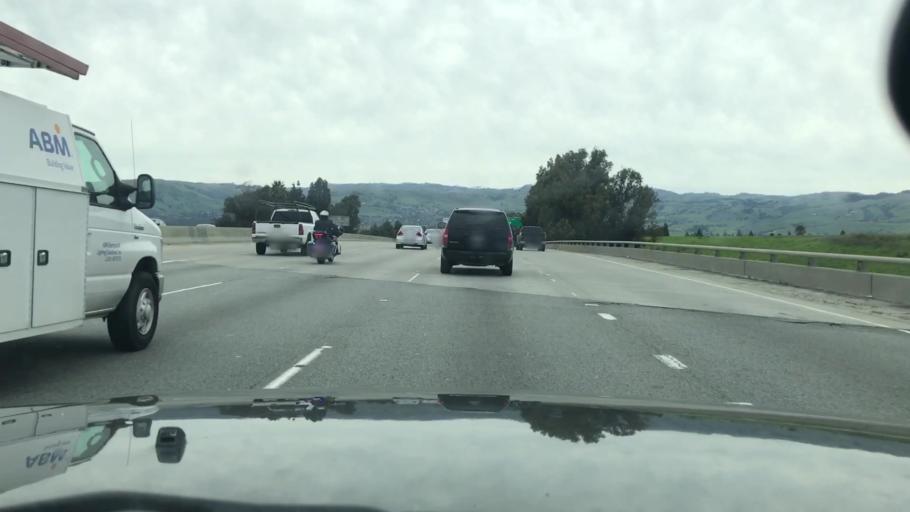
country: US
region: California
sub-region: Santa Clara County
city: San Jose
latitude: 37.3298
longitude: -121.8658
